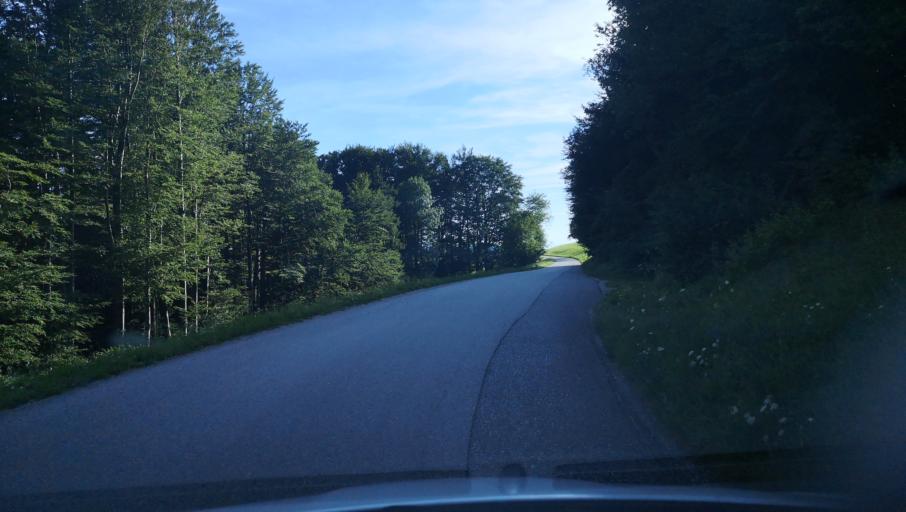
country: AT
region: Lower Austria
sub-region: Politischer Bezirk Amstetten
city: Neuhofen an der Ybbs
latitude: 48.0196
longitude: 14.9041
